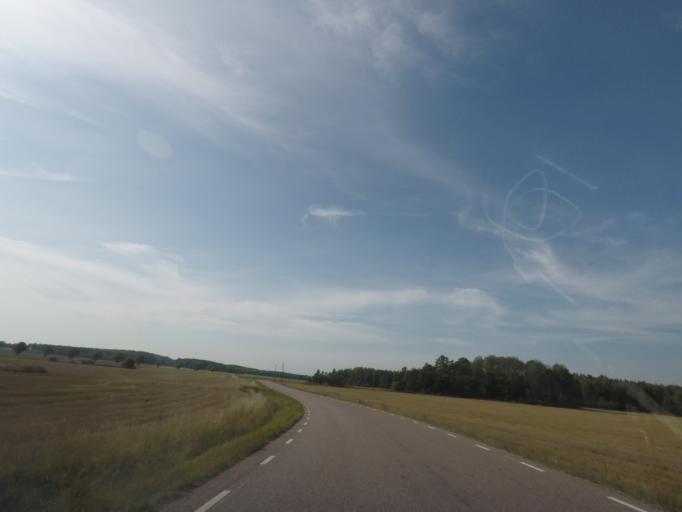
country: SE
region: Vaestmanland
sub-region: Hallstahammars Kommun
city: Kolback
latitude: 59.5244
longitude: 16.1883
